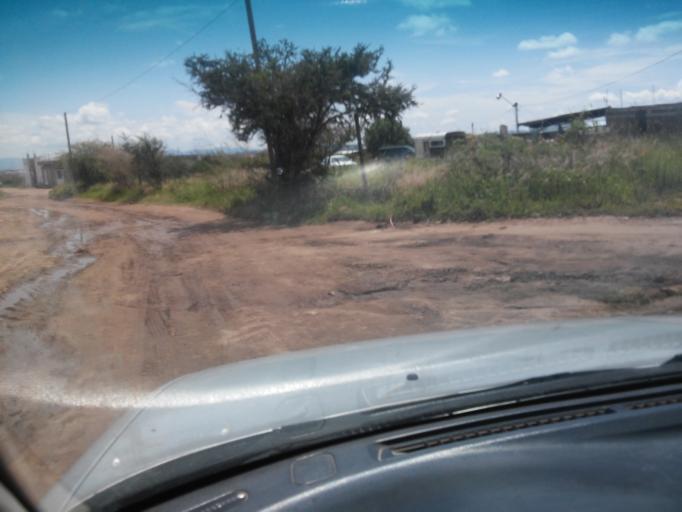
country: MX
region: Durango
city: Victoria de Durango
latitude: 23.9841
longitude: -104.7092
